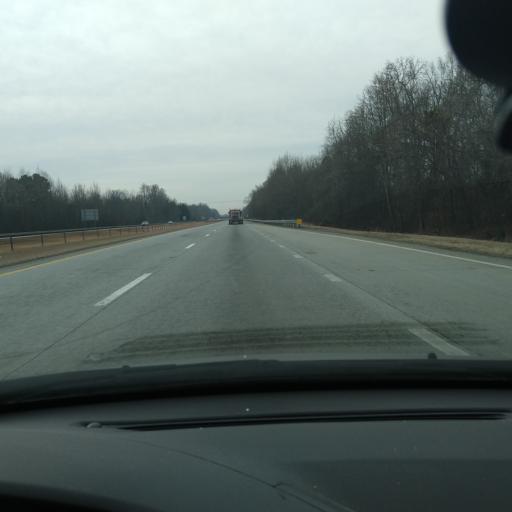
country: US
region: North Carolina
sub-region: Davidson County
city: Lexington
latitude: 35.8305
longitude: -80.2834
